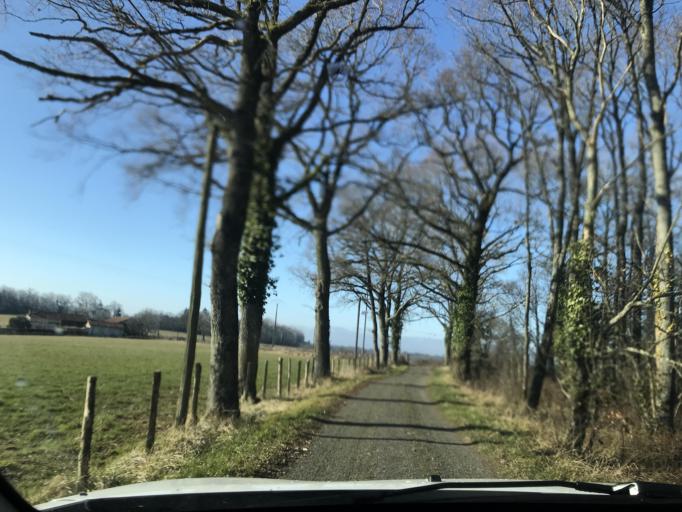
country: FR
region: Poitou-Charentes
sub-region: Departement de la Charente
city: Chasseneuil-sur-Bonnieure
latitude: 45.8387
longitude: 0.5285
